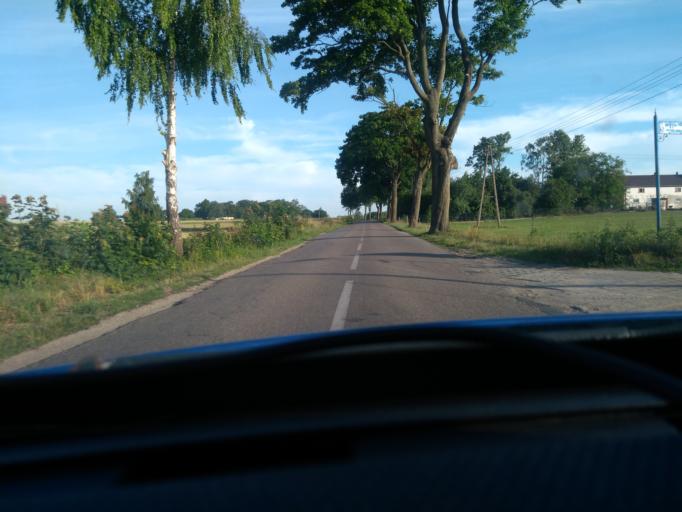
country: PL
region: Pomeranian Voivodeship
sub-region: Powiat kartuski
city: Przodkowo
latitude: 54.3970
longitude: 18.3373
